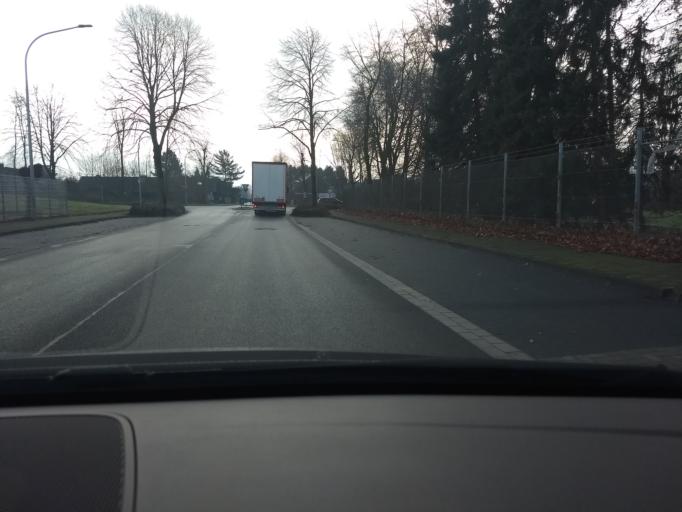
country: DE
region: North Rhine-Westphalia
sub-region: Regierungsbezirk Munster
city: Borken
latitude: 51.8498
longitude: 6.8787
